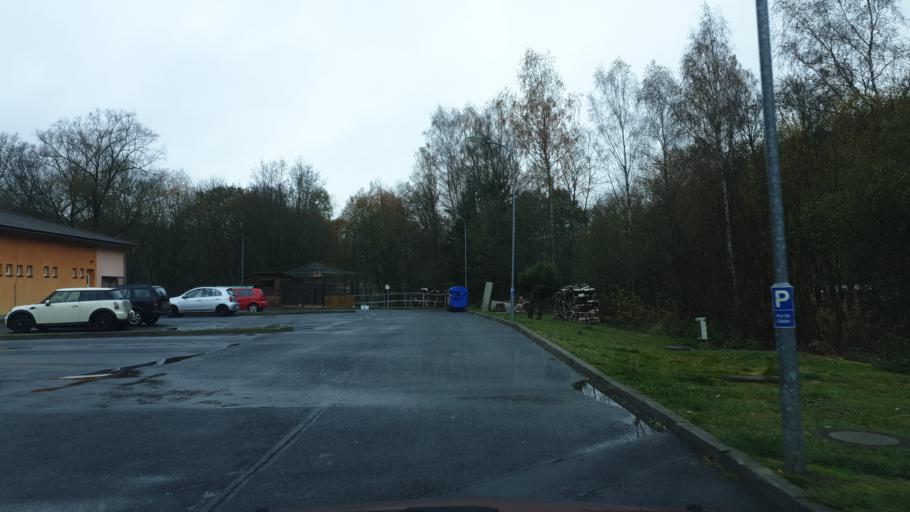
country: DE
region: Saxony
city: Klingenthal
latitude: 50.3507
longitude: 12.4749
